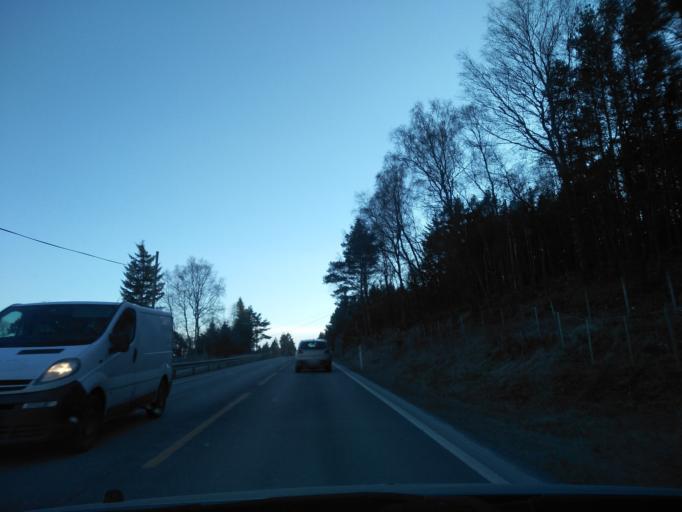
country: NO
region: Rogaland
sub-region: Tysvaer
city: Aksdal
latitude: 59.3893
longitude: 5.4644
